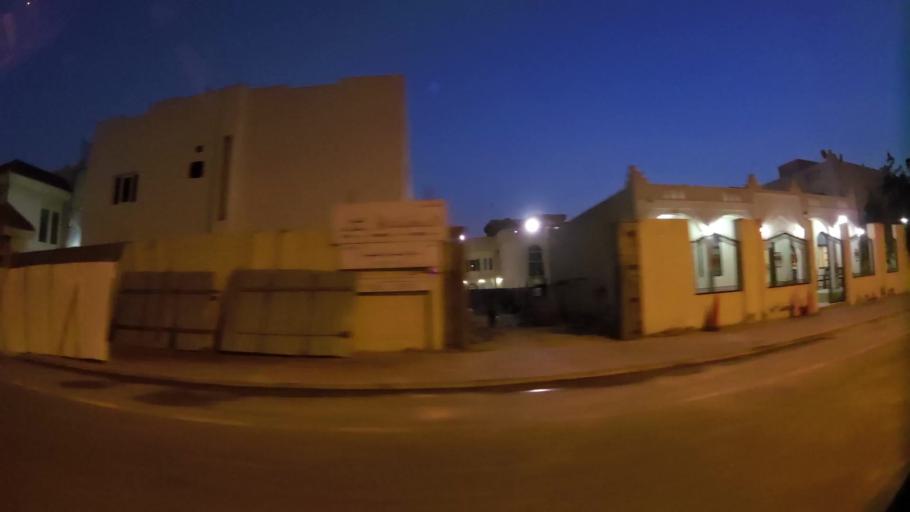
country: QA
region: Baladiyat ad Dawhah
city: Doha
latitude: 25.2568
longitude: 51.4808
